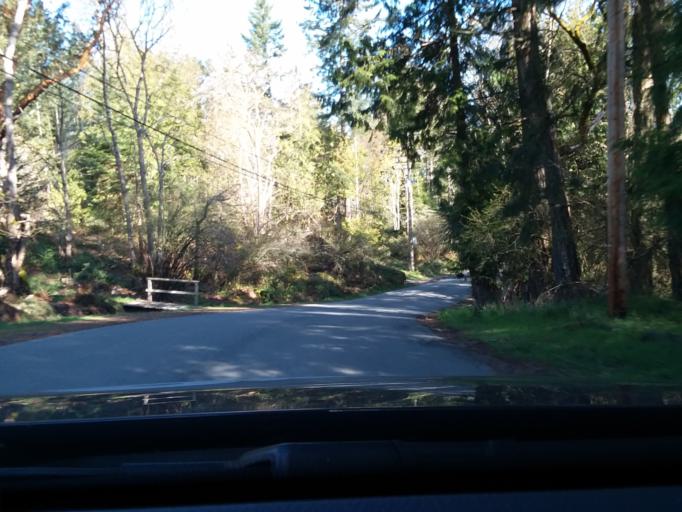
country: CA
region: British Columbia
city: North Saanich
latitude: 48.8774
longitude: -123.3233
